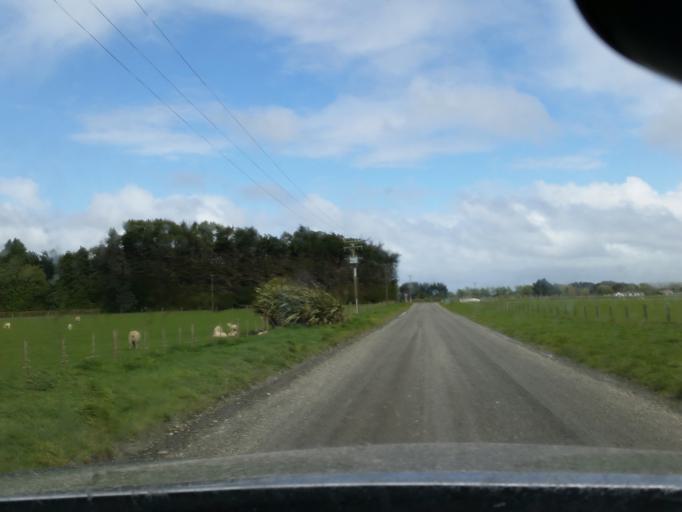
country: NZ
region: Southland
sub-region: Invercargill City
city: Invercargill
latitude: -46.3075
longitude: 168.3033
